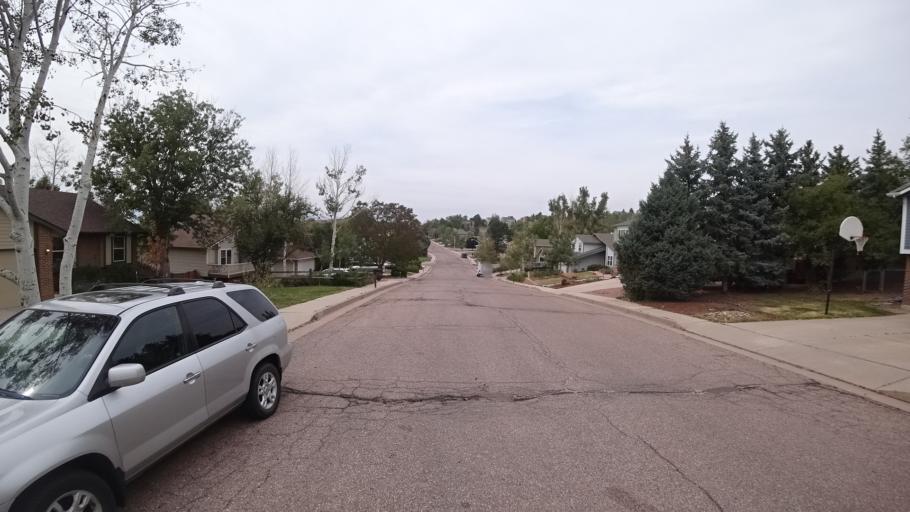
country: US
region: Colorado
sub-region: El Paso County
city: Cimarron Hills
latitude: 38.9063
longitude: -104.7256
